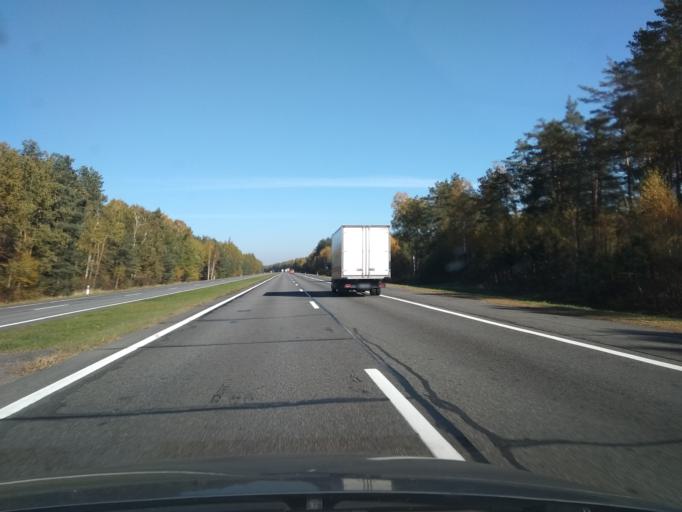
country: BY
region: Brest
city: Ivatsevichy
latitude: 52.7644
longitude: 25.5266
